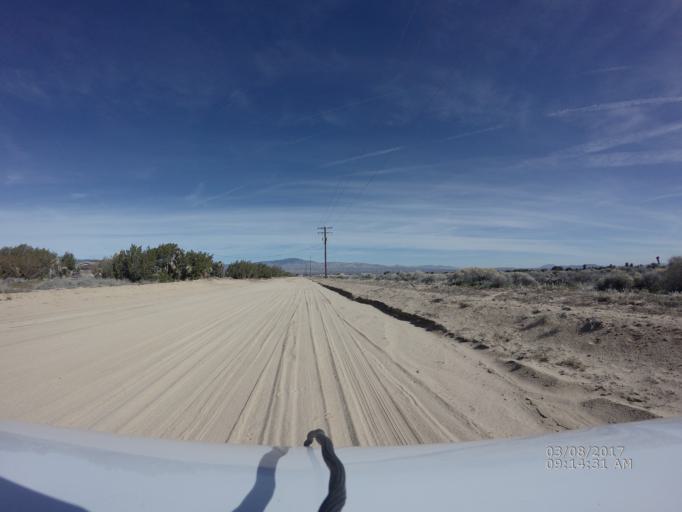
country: US
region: California
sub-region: Los Angeles County
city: Green Valley
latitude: 34.7657
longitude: -118.4666
